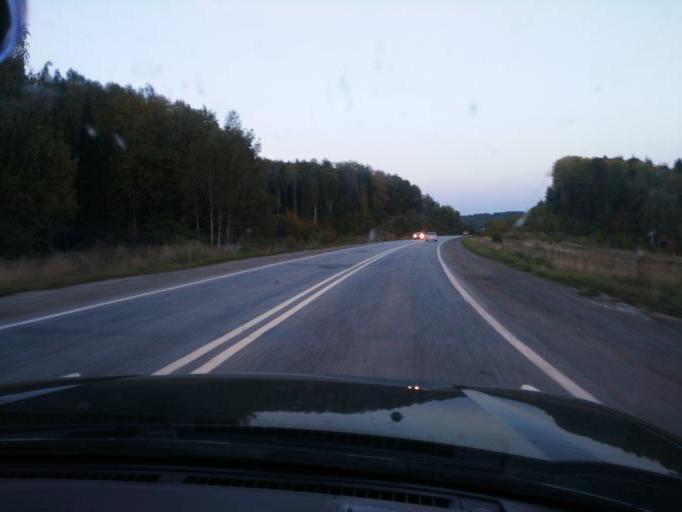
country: RU
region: Perm
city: Verkhnechusovskiye Gorodki
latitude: 58.2960
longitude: 56.8663
